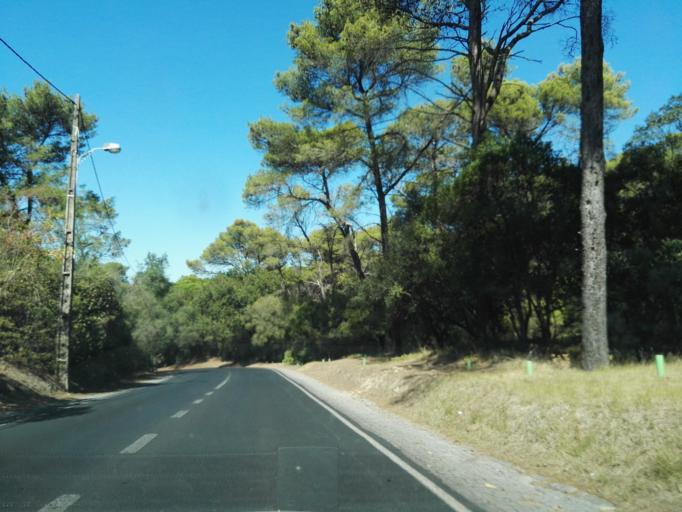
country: PT
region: Lisbon
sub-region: Odivelas
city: Pontinha
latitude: 38.7325
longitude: -9.1980
